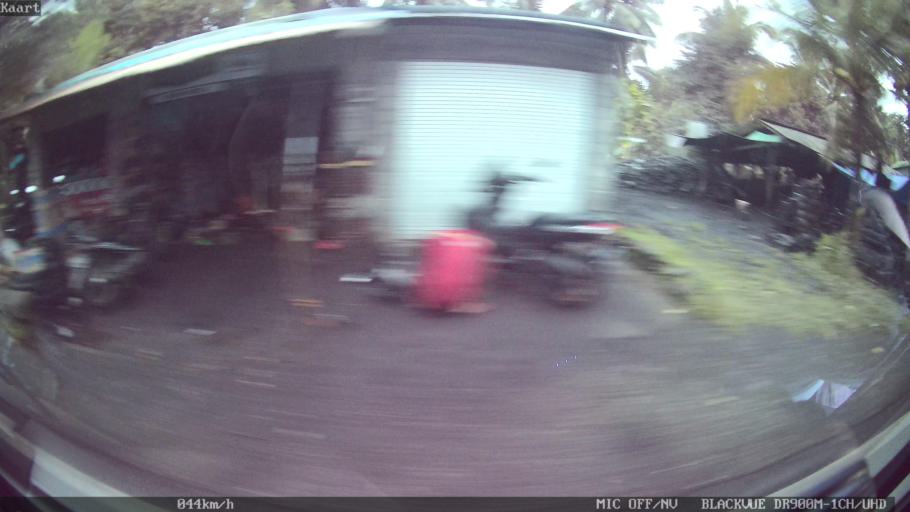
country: ID
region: Bali
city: Pohgending Kawan
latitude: -8.4463
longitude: 115.1401
